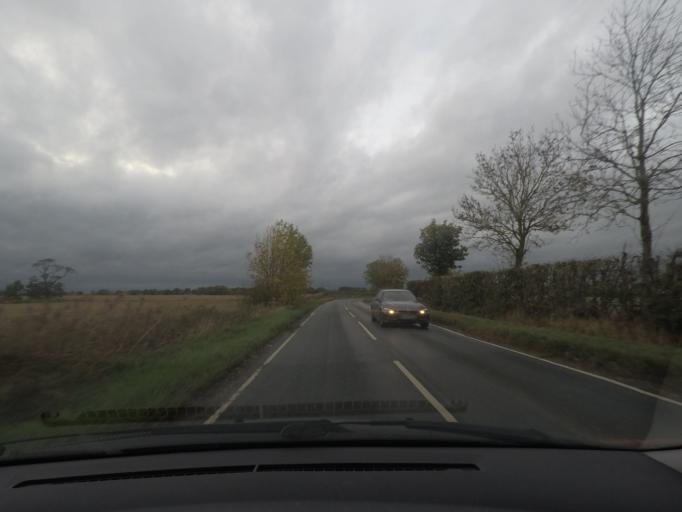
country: GB
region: England
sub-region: City of York
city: Wigginton
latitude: 54.0815
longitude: -1.1084
